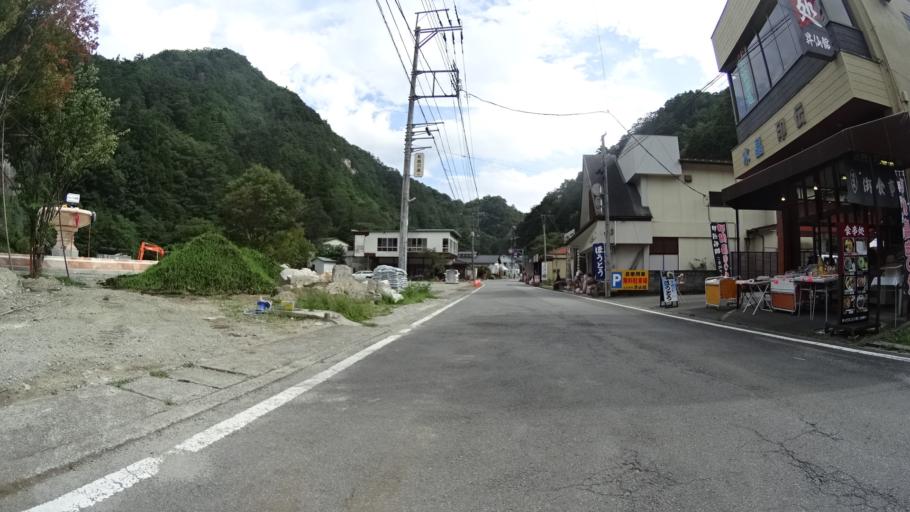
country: JP
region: Yamanashi
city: Kofu-shi
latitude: 35.7528
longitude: 138.5649
